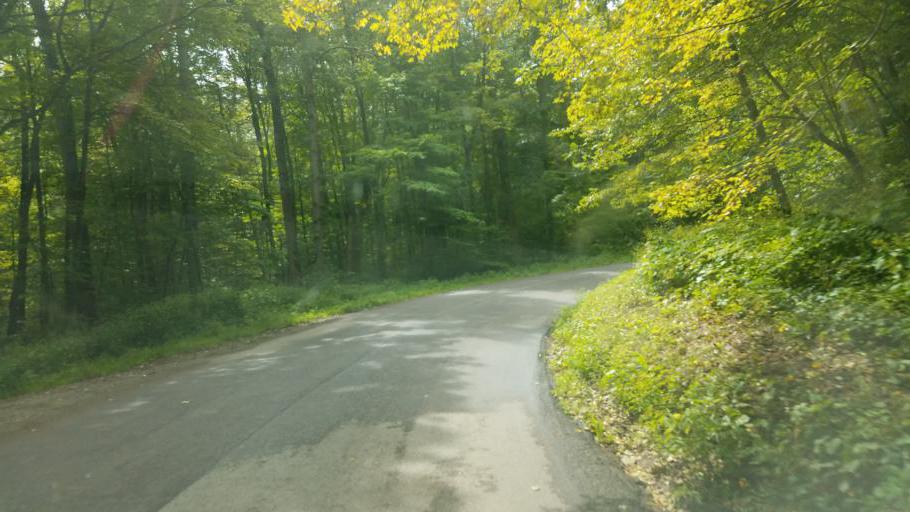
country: US
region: Ohio
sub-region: Ashland County
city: Loudonville
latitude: 40.5597
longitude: -82.3563
